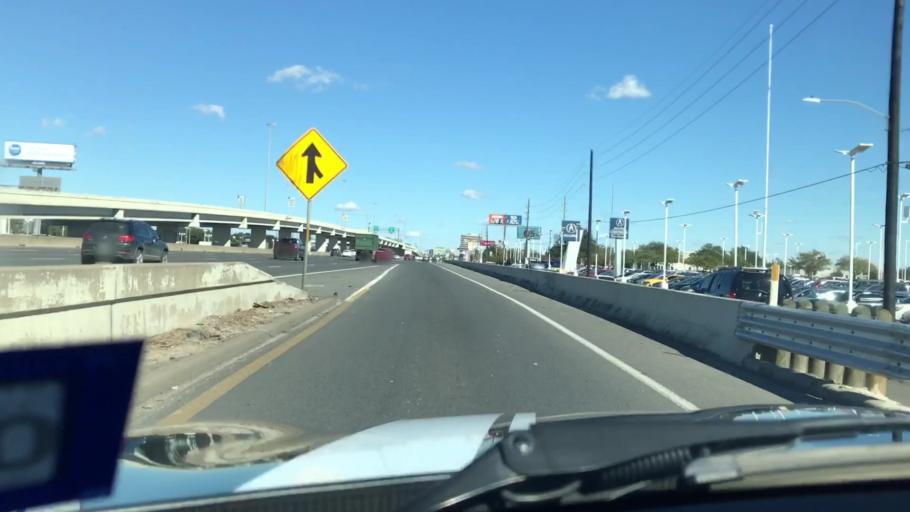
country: US
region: Texas
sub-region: Fort Bend County
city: Meadows Place
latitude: 29.6673
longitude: -95.5507
